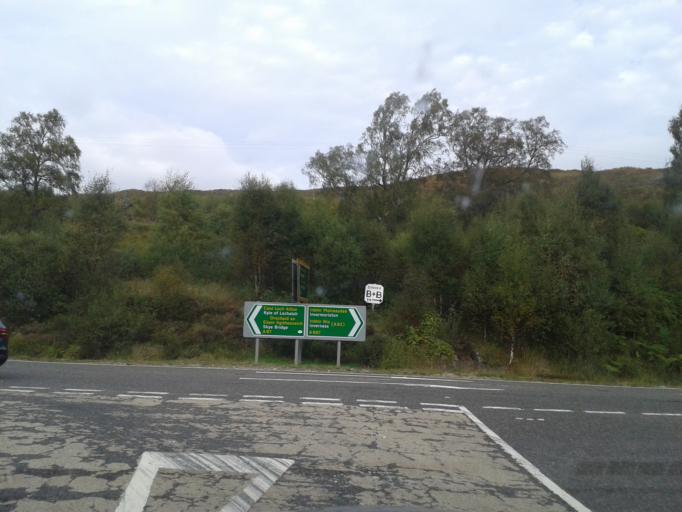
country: GB
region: Scotland
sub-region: Highland
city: Spean Bridge
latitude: 57.1460
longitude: -4.9586
